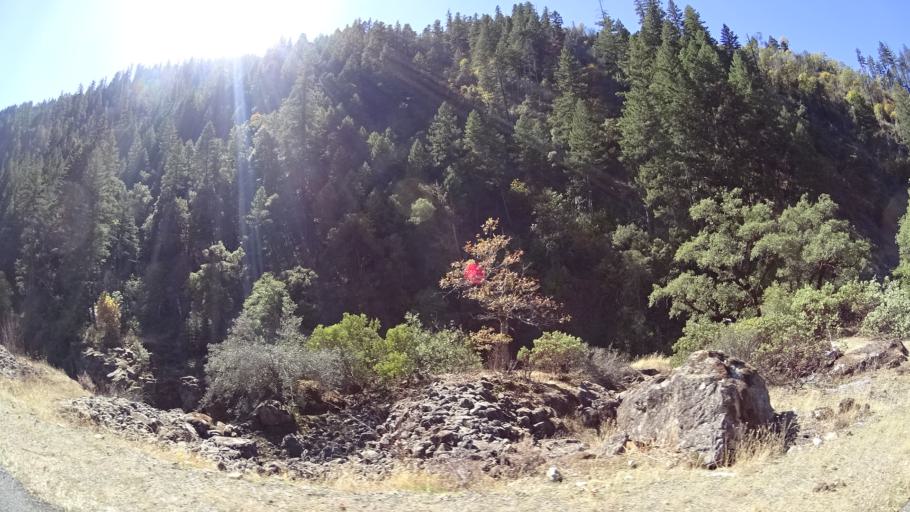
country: US
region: California
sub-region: Humboldt County
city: Willow Creek
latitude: 41.2867
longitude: -123.3648
